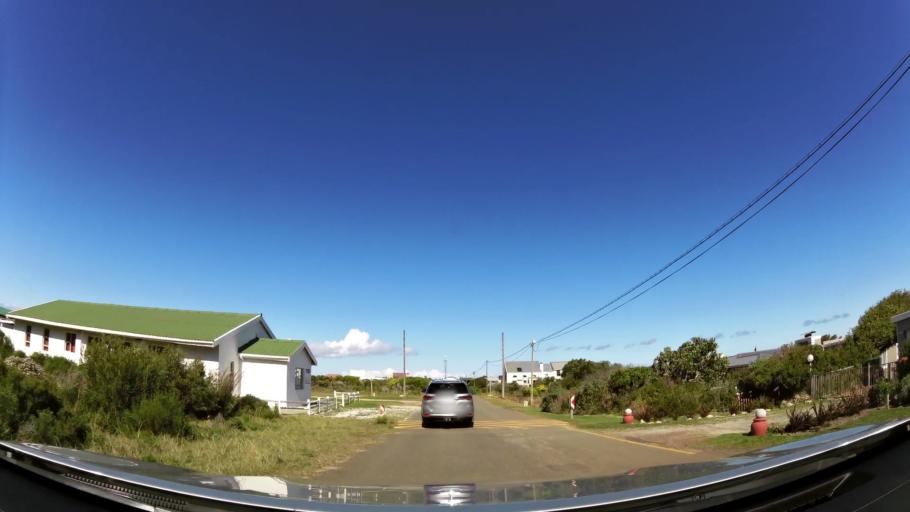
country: ZA
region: Western Cape
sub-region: Overberg District Municipality
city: Grabouw
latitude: -34.3674
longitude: 18.8910
